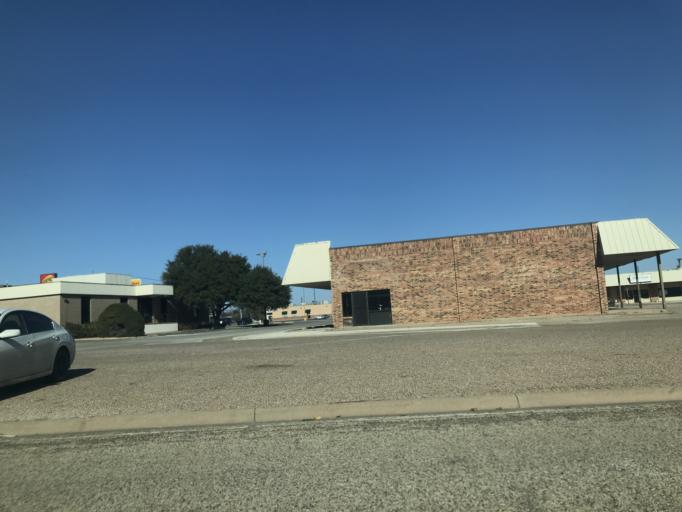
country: US
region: Texas
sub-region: Taylor County
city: Abilene
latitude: 32.4569
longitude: -99.7048
